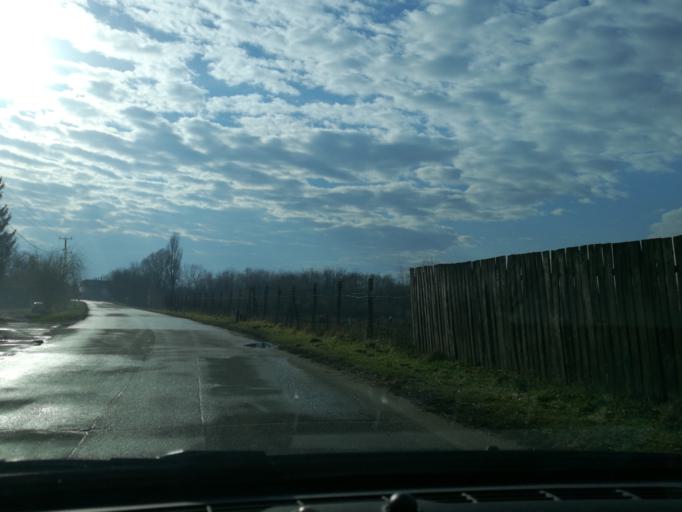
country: HU
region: Szabolcs-Szatmar-Bereg
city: Nyirpazony
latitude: 47.9471
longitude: 21.7980
